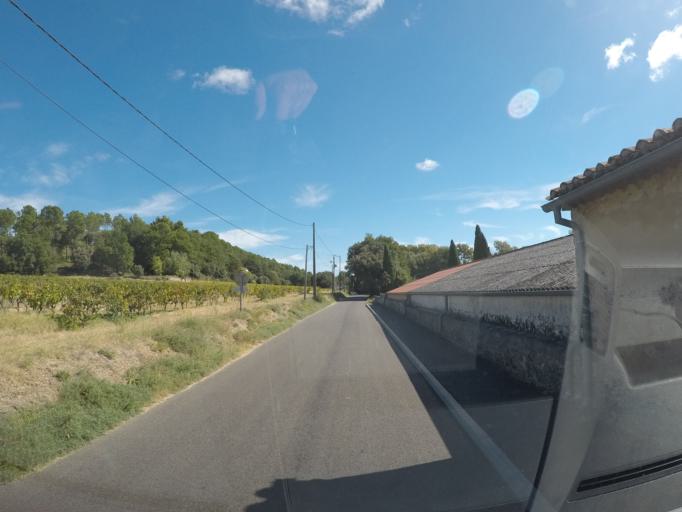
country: FR
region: Provence-Alpes-Cote d'Azur
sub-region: Departement du Vaucluse
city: Bollene
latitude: 44.2872
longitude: 4.7904
